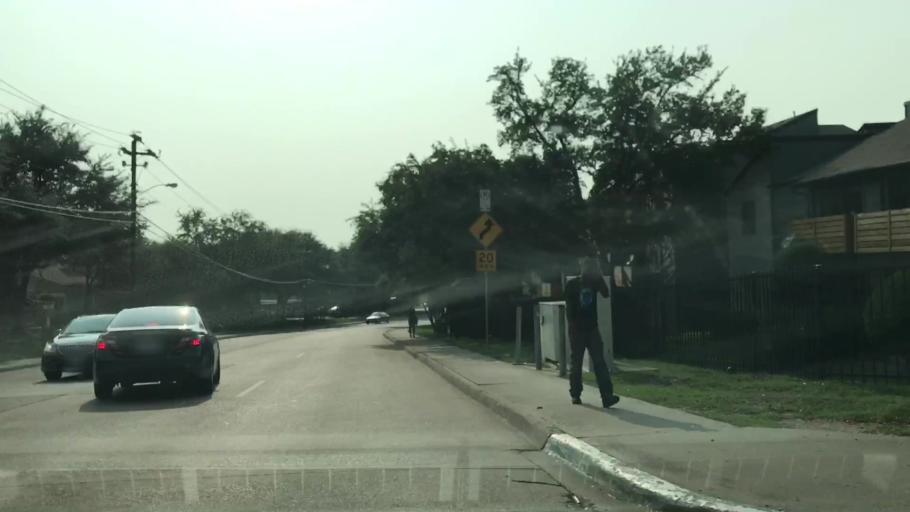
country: US
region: Texas
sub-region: Dallas County
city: Richardson
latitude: 32.8999
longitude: -96.7236
